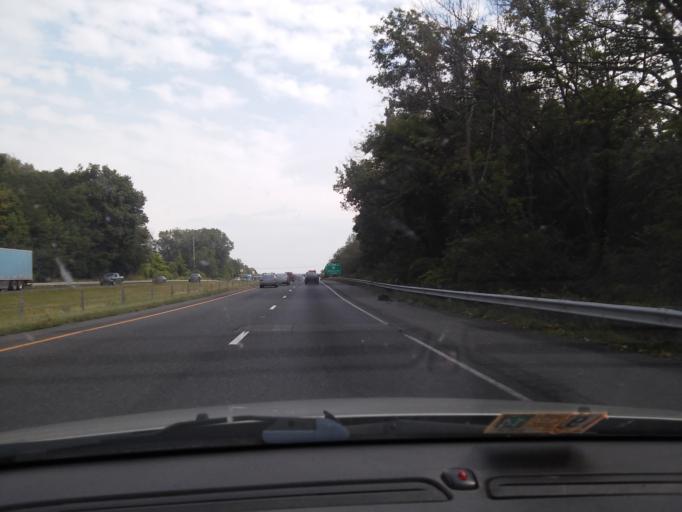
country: US
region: Ohio
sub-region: Preble County
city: New Paris
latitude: 39.8591
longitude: -84.8444
